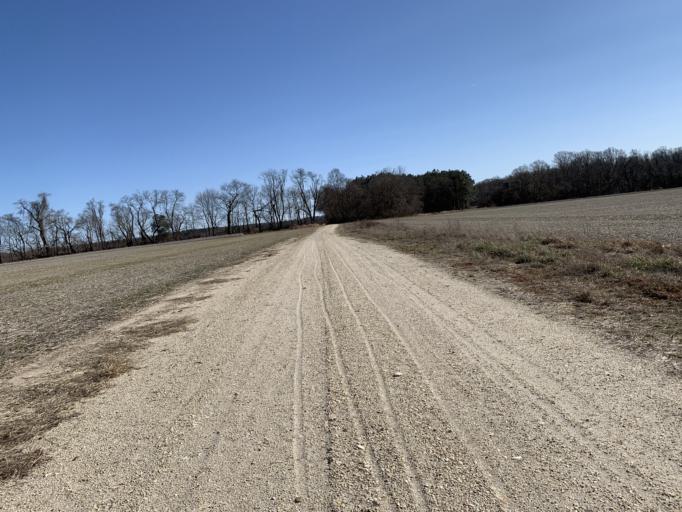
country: US
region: Delaware
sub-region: Kent County
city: Riverview
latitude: 39.0053
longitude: -75.4280
